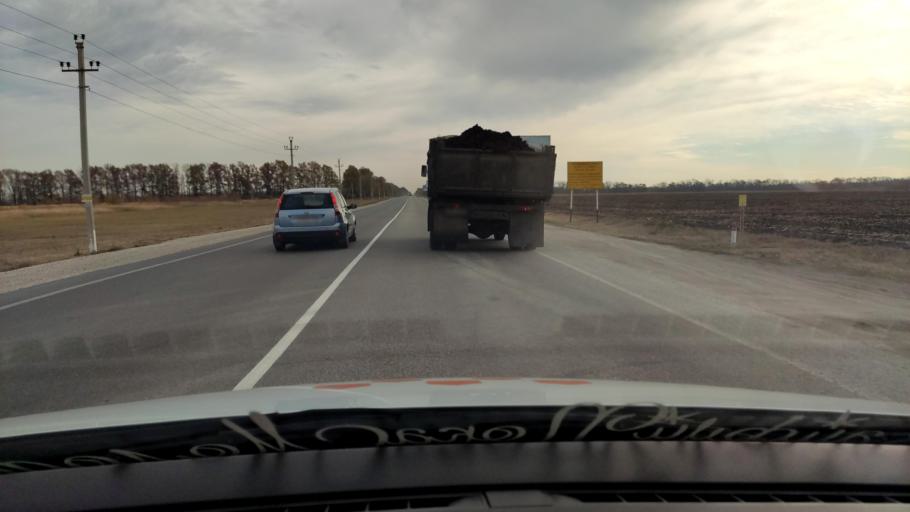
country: RU
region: Voronezj
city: Ramon'
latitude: 51.9294
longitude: 39.2282
